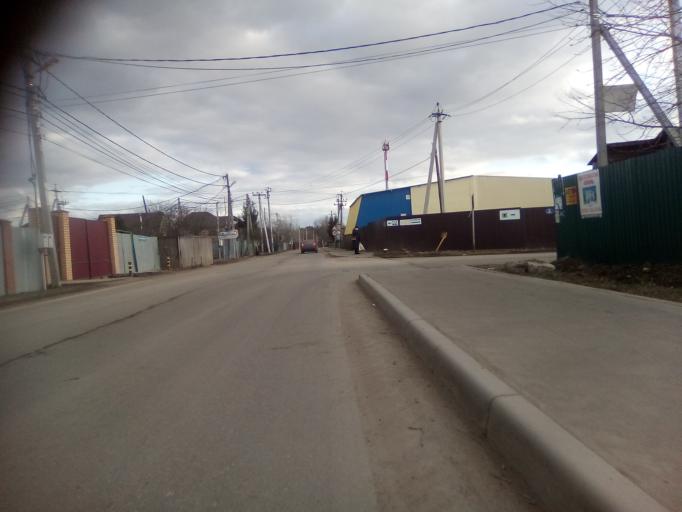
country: RU
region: Moskovskaya
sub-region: Leninskiy Rayon
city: Vnukovo
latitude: 55.5932
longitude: 37.3198
